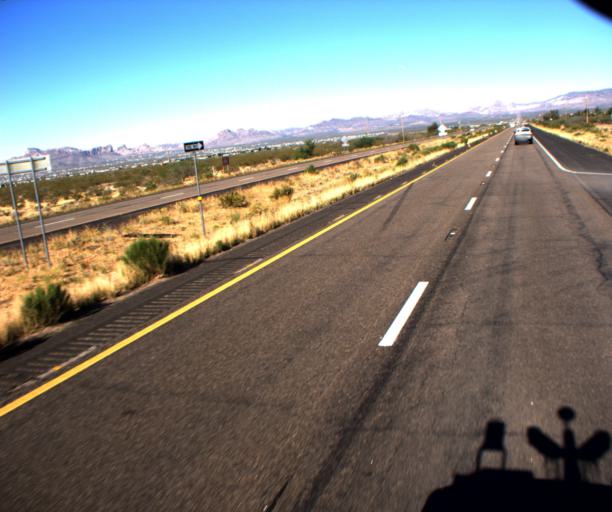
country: US
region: Arizona
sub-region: Mohave County
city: Golden Valley
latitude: 35.2232
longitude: -114.2382
